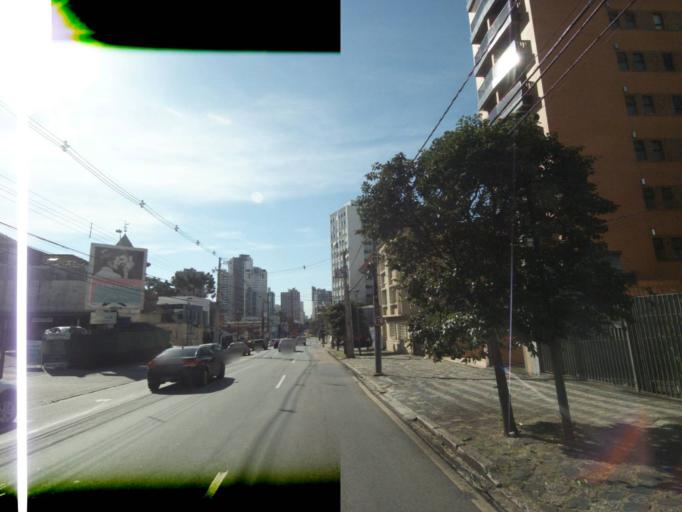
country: BR
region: Parana
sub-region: Curitiba
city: Curitiba
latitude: -25.4371
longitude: -49.2865
